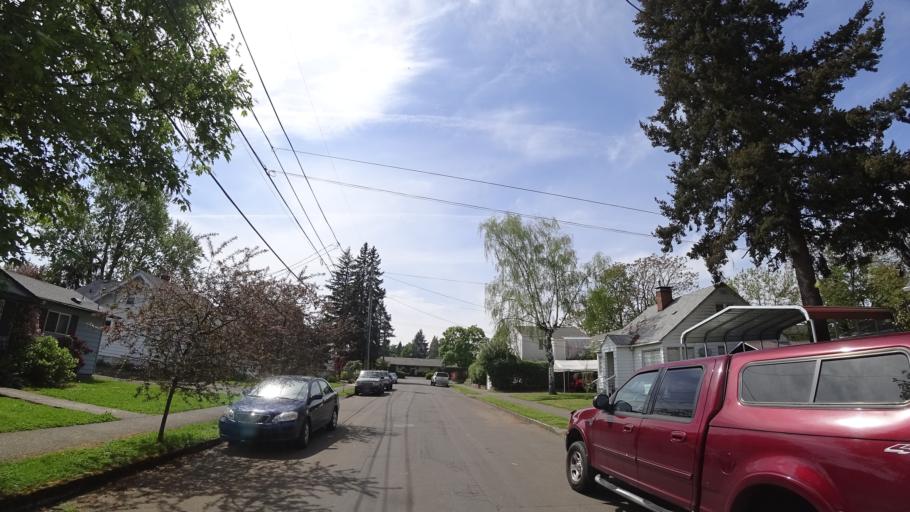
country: US
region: Oregon
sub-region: Multnomah County
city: Lents
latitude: 45.4775
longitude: -122.6078
